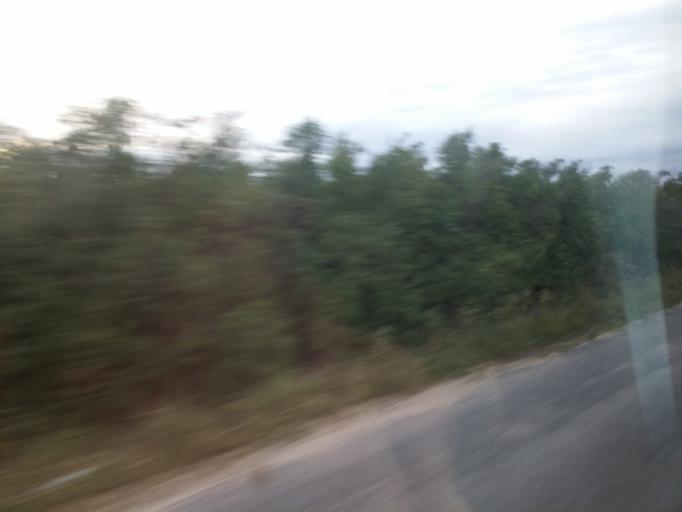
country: HU
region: Veszprem
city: Varpalota
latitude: 47.2167
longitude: 18.1507
